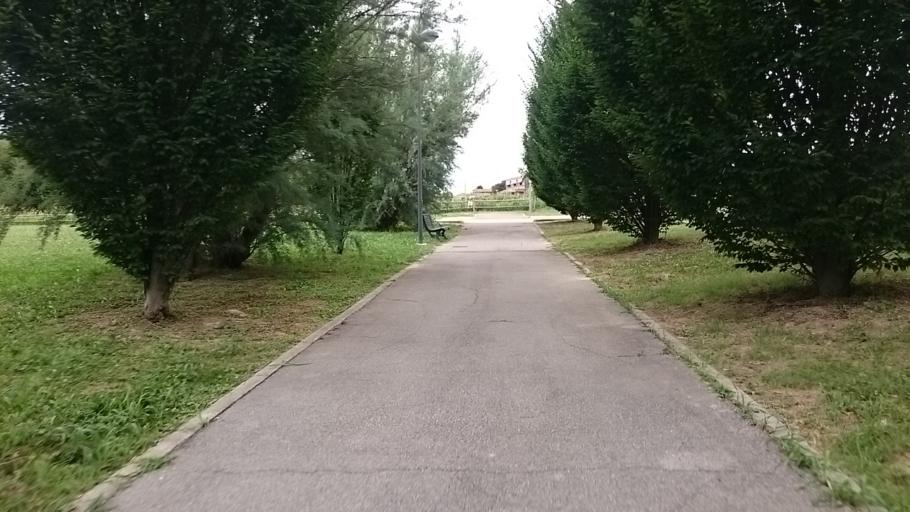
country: IT
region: Veneto
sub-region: Provincia di Padova
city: Albignasego
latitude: 45.3474
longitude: 11.8756
